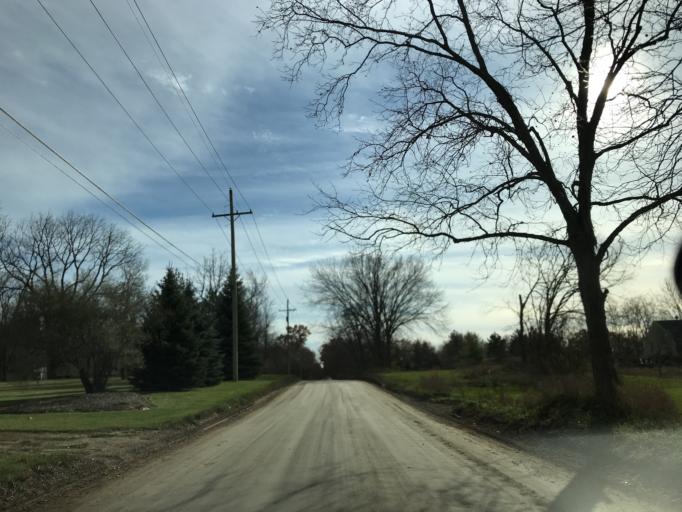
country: US
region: Michigan
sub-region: Oakland County
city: South Lyon
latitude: 42.4860
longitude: -83.6382
